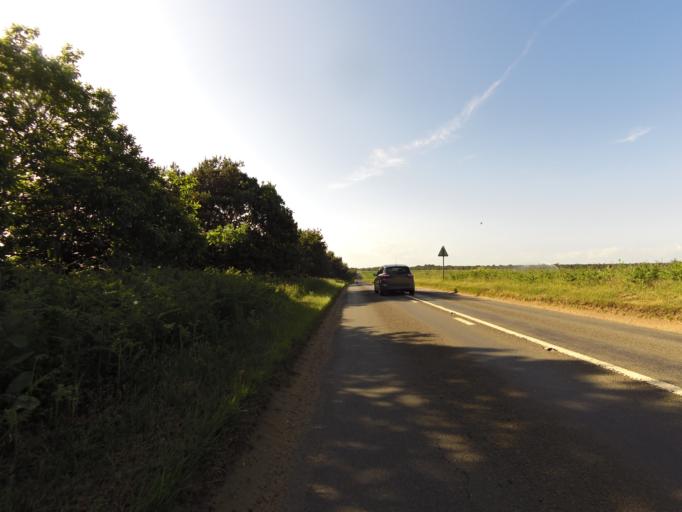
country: GB
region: England
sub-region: Suffolk
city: Woodbridge
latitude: 52.0792
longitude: 1.3627
